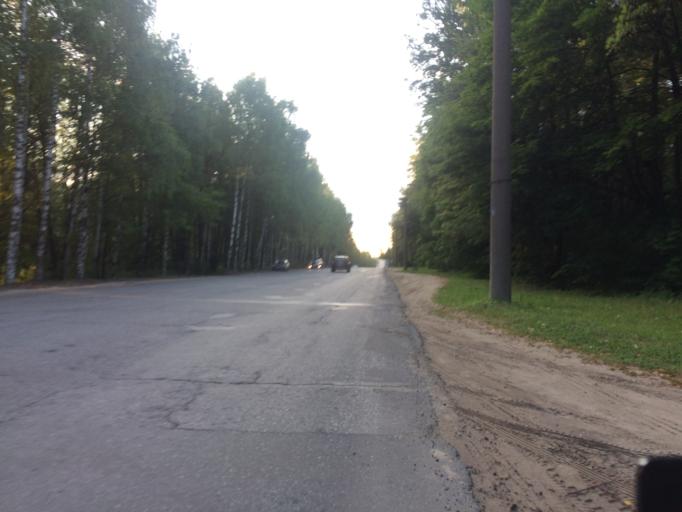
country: RU
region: Mariy-El
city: Yoshkar-Ola
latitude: 56.6236
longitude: 47.9545
